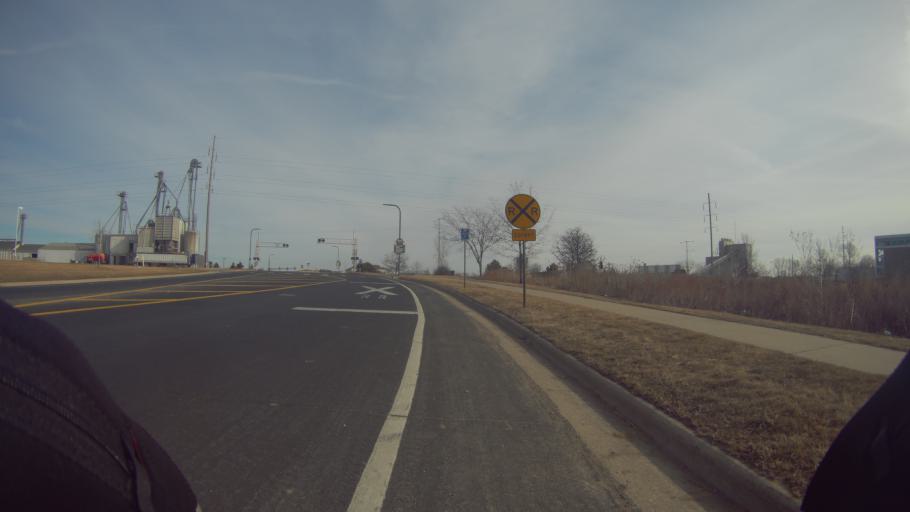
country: US
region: Wisconsin
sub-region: Dane County
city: Middleton
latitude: 43.0951
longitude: -89.5238
